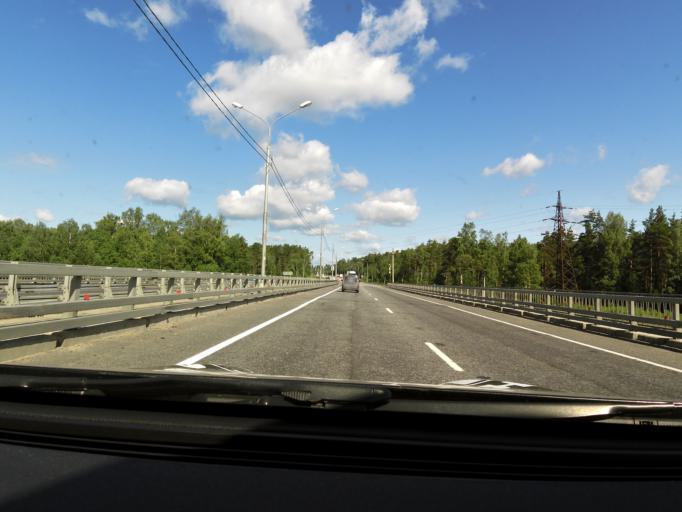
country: RU
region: Tverskaya
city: Likhoslavl'
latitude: 56.9378
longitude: 35.5123
